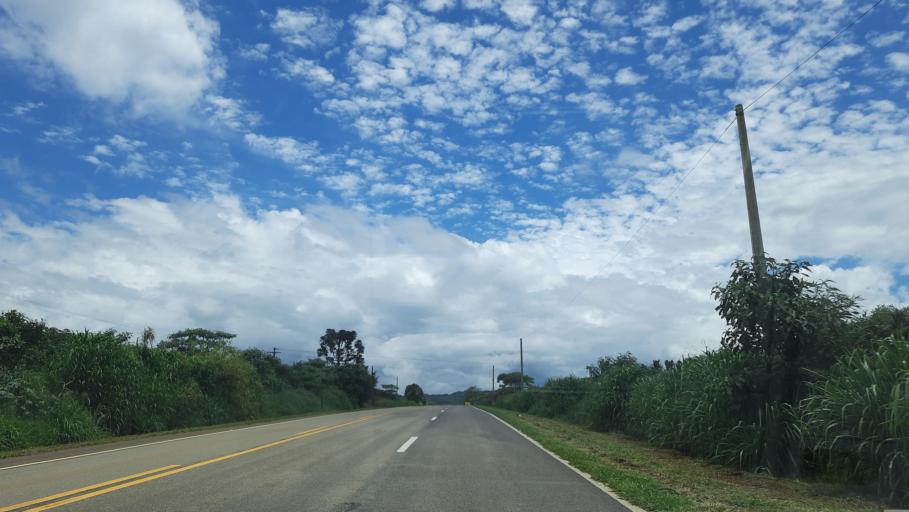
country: BR
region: Sao Paulo
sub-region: Vargem Grande Do Sul
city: Vargem Grande do Sul
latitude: -21.8092
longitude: -46.7906
